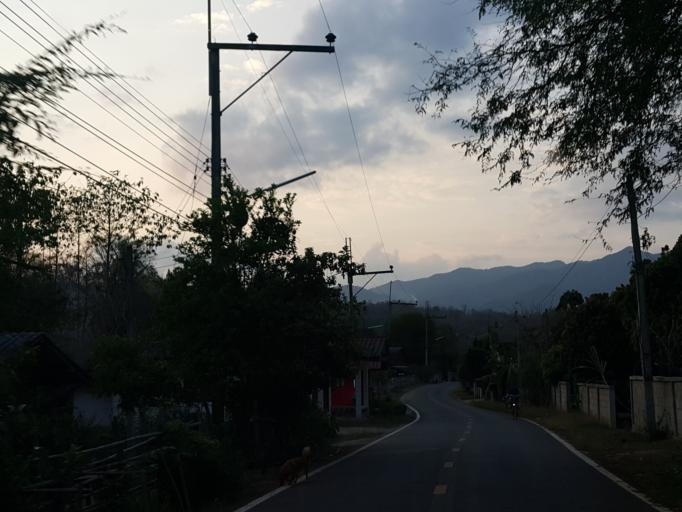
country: TH
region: Lampang
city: Mueang Pan
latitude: 18.7884
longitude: 99.4946
